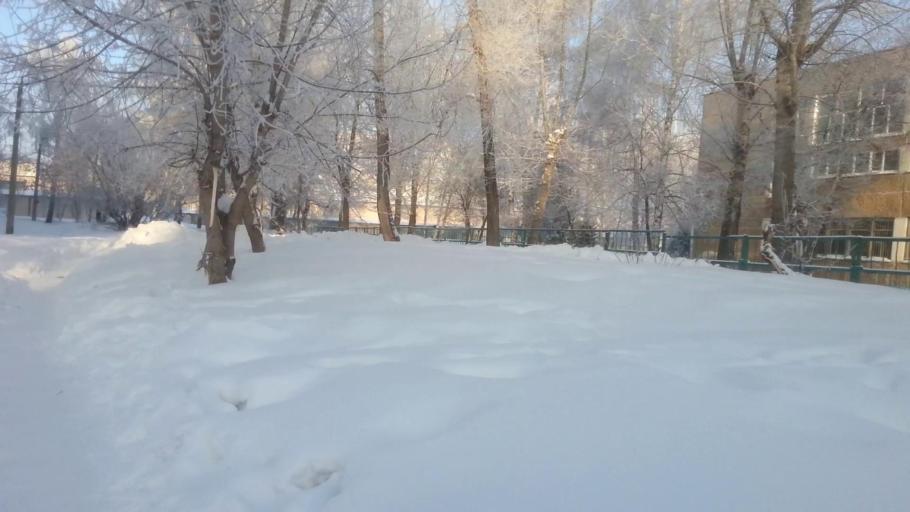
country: RU
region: Altai Krai
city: Novosilikatnyy
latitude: 53.3778
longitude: 83.6732
